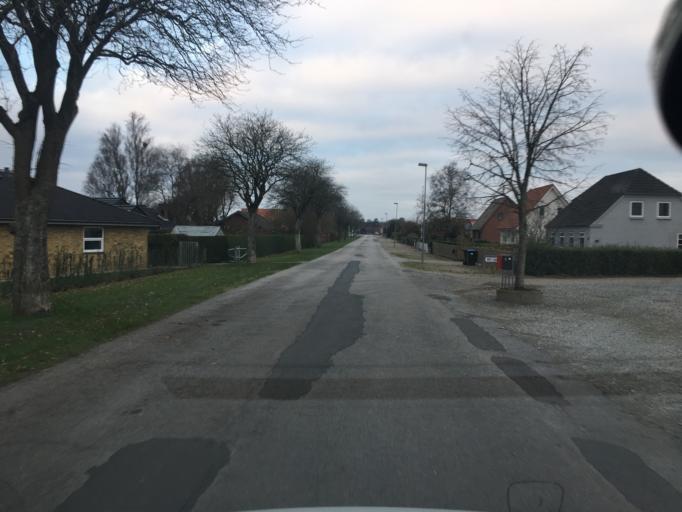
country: DK
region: South Denmark
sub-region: Tonder Kommune
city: Logumkloster
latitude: 55.0562
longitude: 8.9677
